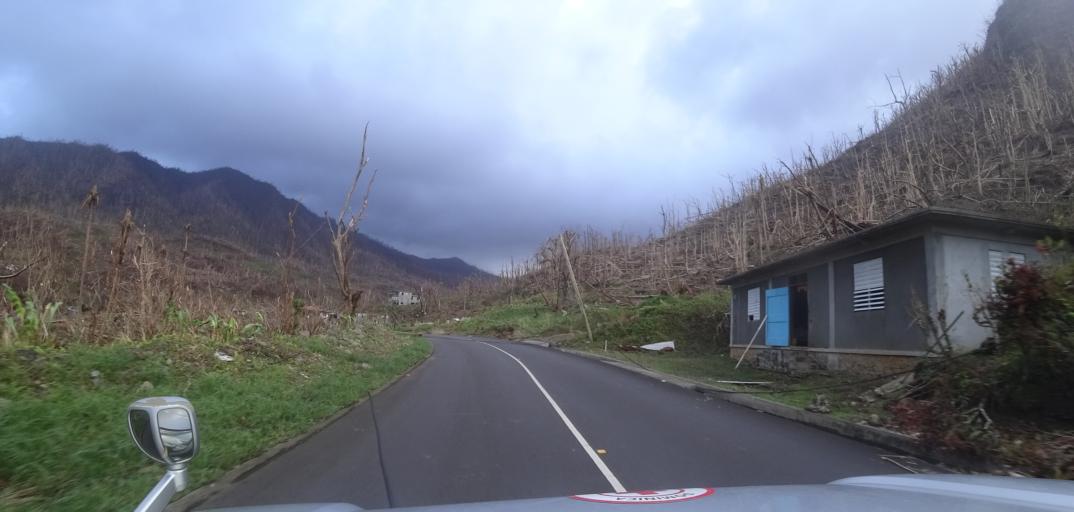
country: DM
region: Saint Andrew
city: Marigot
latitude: 15.4888
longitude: -61.2777
